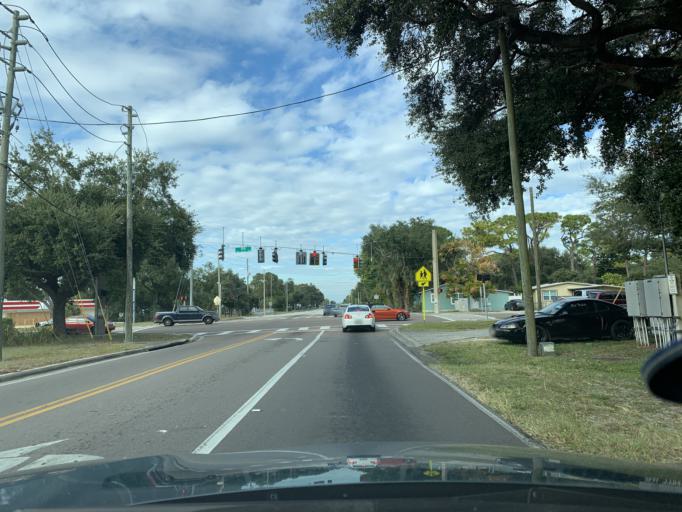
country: US
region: Florida
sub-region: Pinellas County
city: Kenneth City
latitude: 27.8206
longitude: -82.7367
